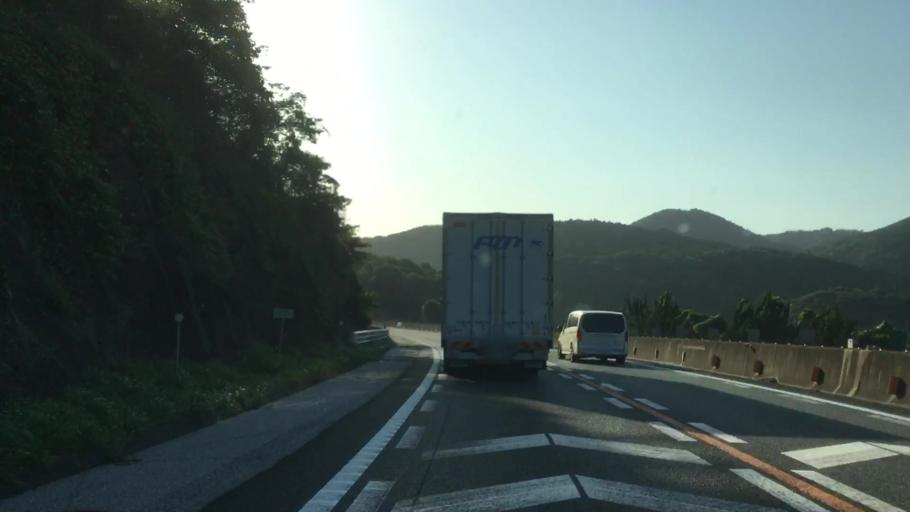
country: JP
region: Yamaguchi
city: Onoda
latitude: 34.1194
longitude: 131.1876
